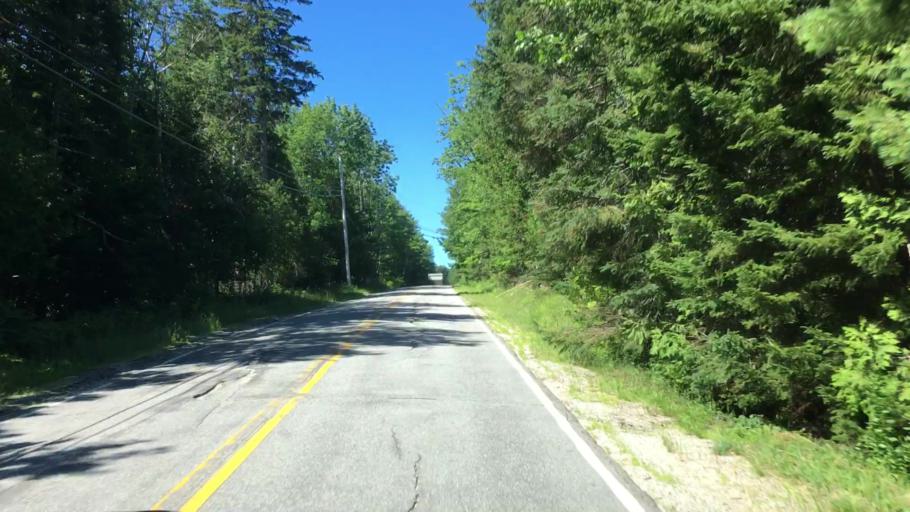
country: US
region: Maine
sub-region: Hancock County
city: Sedgwick
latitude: 44.3273
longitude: -68.6019
